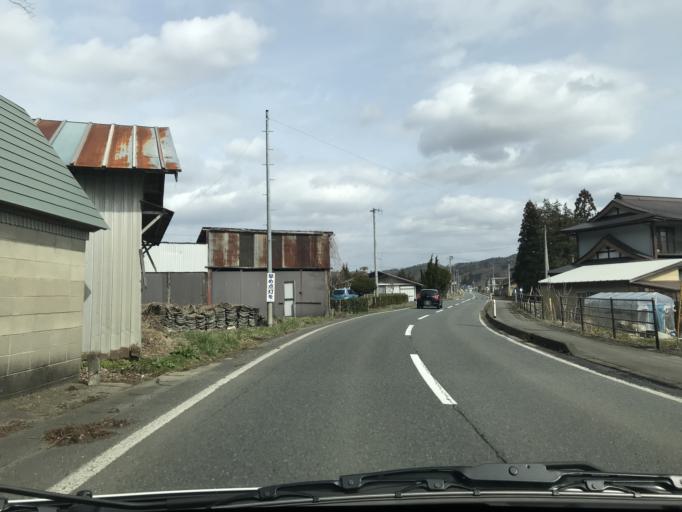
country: JP
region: Iwate
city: Mizusawa
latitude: 39.1987
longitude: 141.1861
